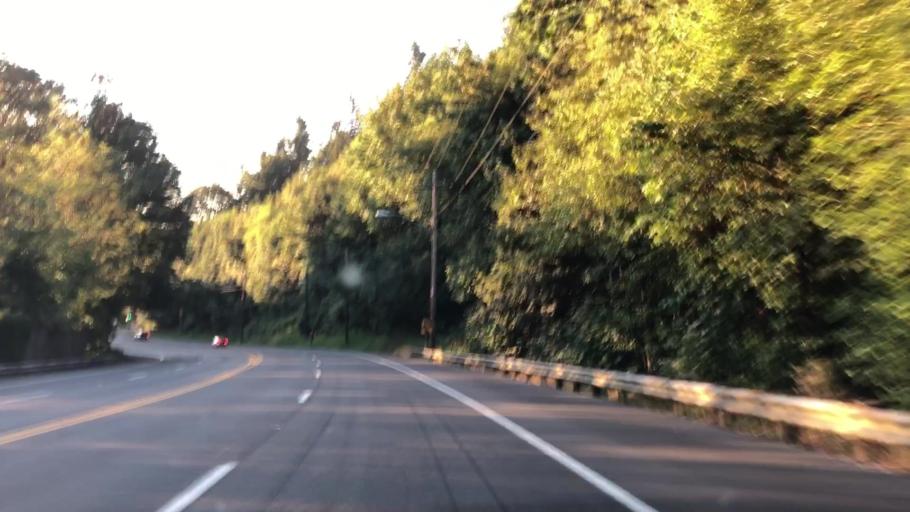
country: US
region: Washington
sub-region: King County
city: Lakeland North
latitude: 47.3544
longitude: -122.2674
